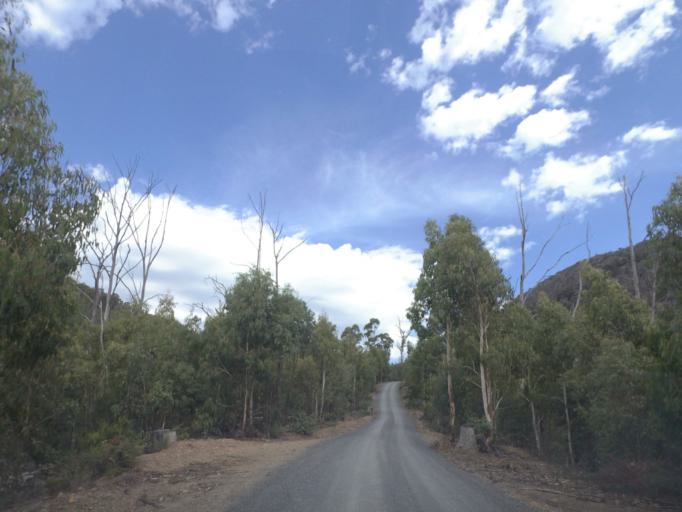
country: AU
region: Victoria
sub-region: Murrindindi
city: Alexandra
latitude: -37.4044
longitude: 145.7579
